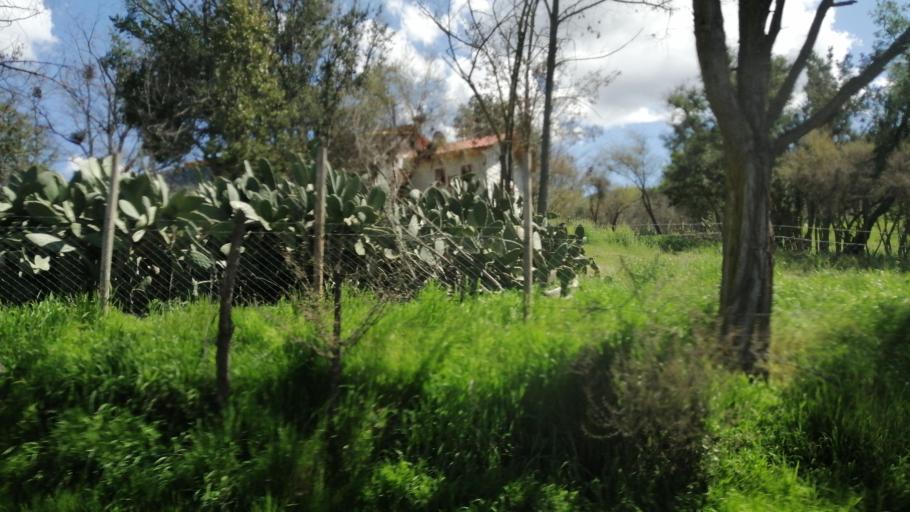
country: CL
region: Valparaiso
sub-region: Provincia de Marga Marga
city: Limache
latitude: -33.1866
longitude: -71.1910
